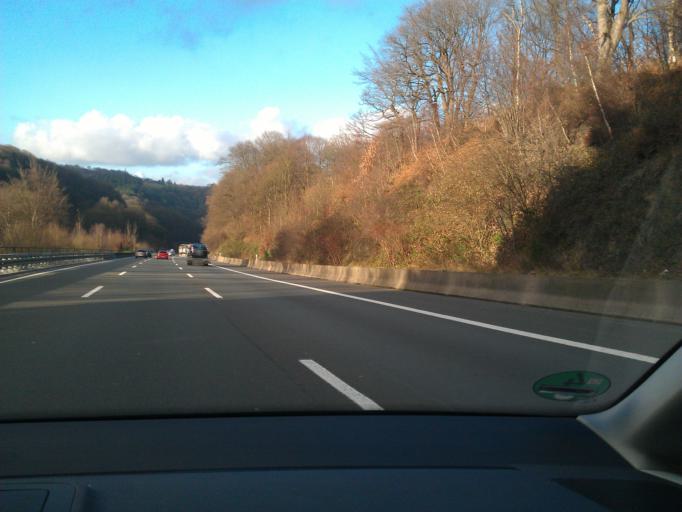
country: DE
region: North Rhine-Westphalia
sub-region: Regierungsbezirk Dusseldorf
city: Wuppertal
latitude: 51.2413
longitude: 7.2300
